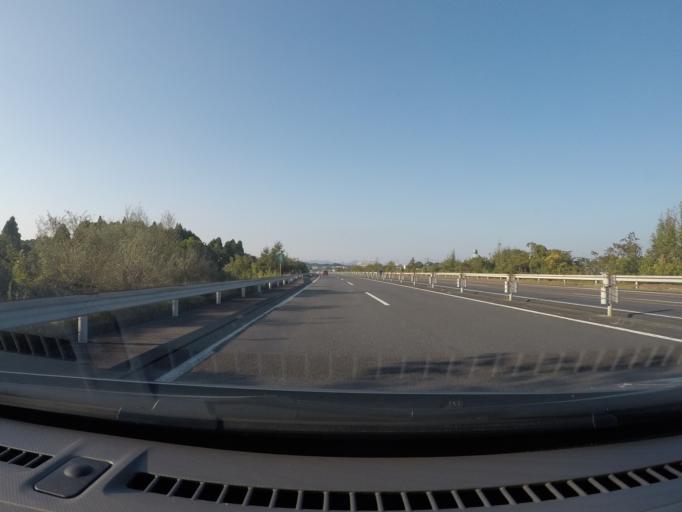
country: JP
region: Kagoshima
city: Kajiki
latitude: 31.7968
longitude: 130.7150
